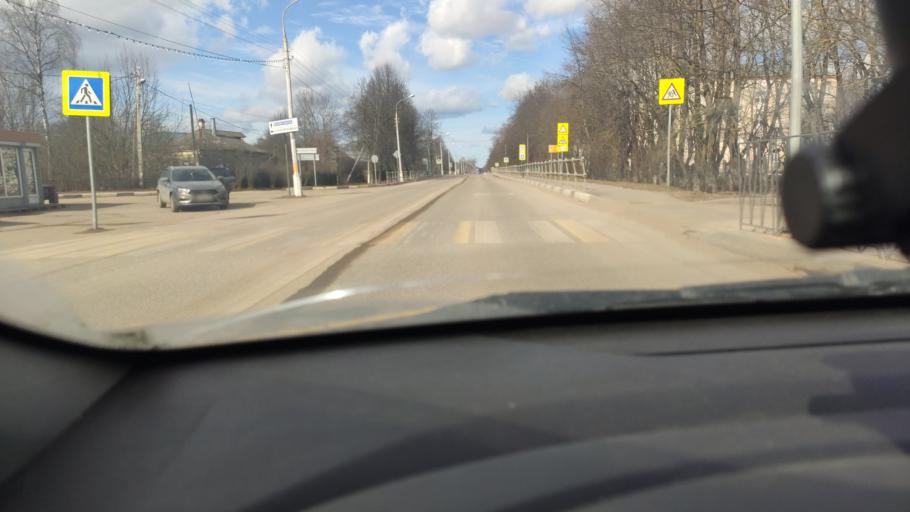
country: RU
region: Moskovskaya
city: Ruza
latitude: 55.7045
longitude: 36.1890
